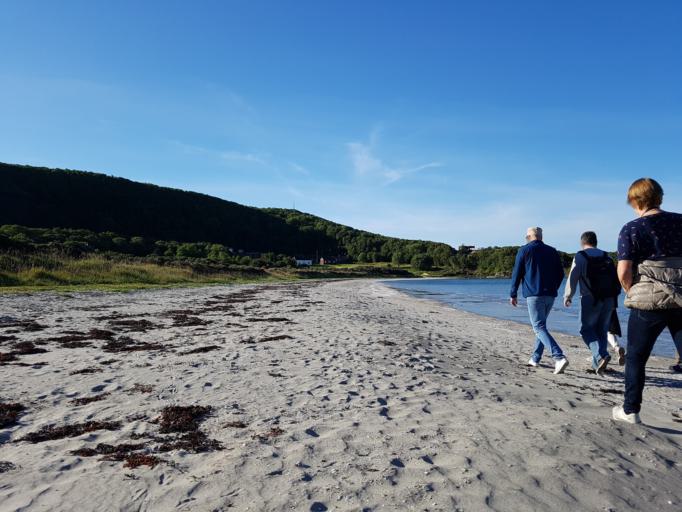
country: NO
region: Sor-Trondelag
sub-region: Afjord
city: A i Afjord
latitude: 64.0530
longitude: 9.9498
